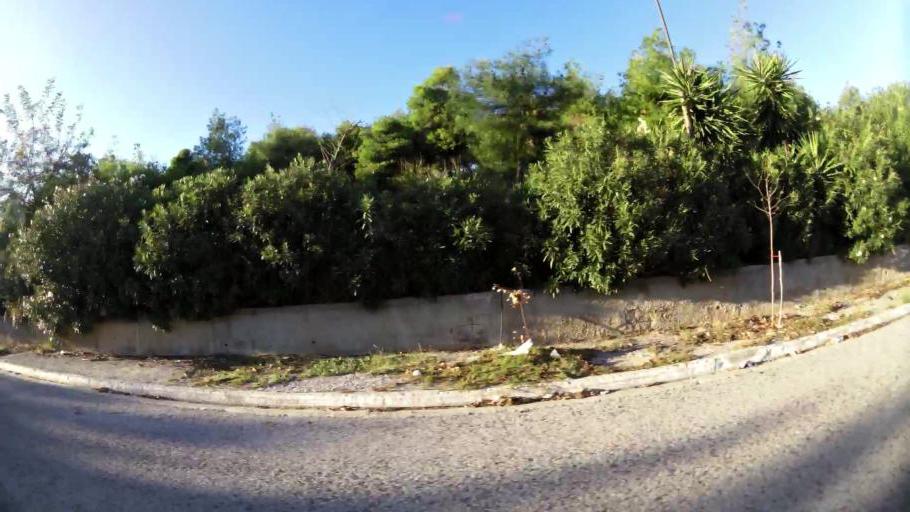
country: GR
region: Attica
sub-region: Nomarchia Anatolikis Attikis
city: Acharnes
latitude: 38.0821
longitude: 23.7234
